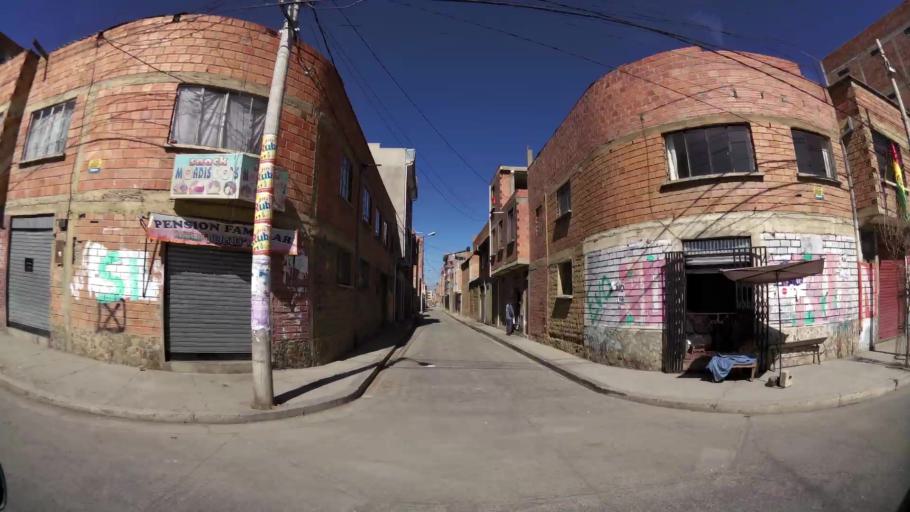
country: BO
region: La Paz
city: La Paz
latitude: -16.5194
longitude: -68.1601
